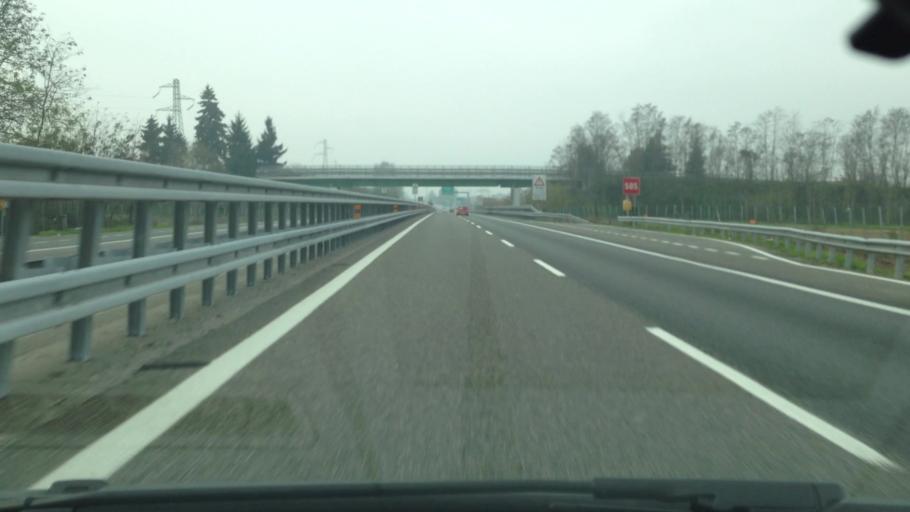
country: IT
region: Piedmont
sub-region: Provincia di Torino
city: Cambiano
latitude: 44.9595
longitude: 7.7942
